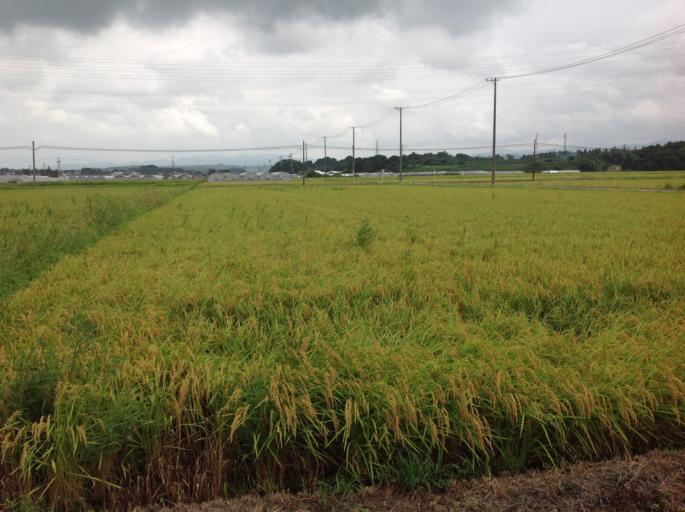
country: JP
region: Shizuoka
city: Fukuroi
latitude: 34.7690
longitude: 137.9636
